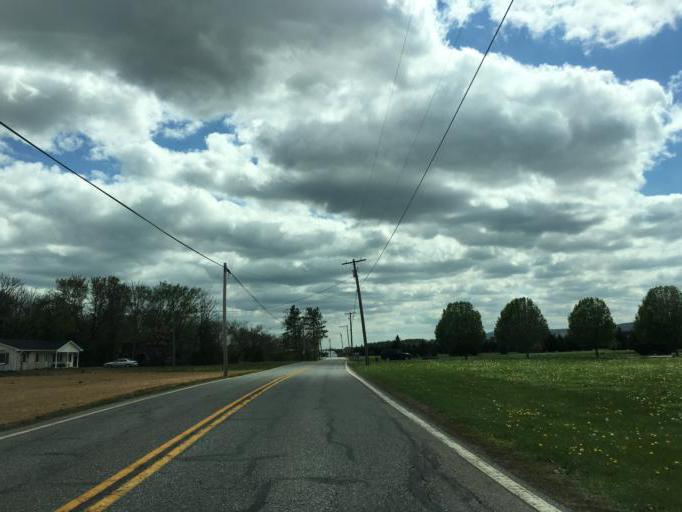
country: US
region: Maryland
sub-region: Frederick County
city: Thurmont
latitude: 39.6050
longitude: -77.3918
